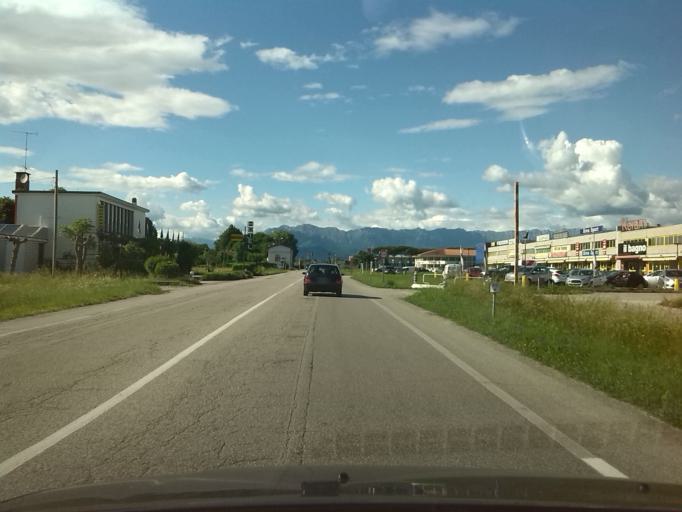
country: IT
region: Friuli Venezia Giulia
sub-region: Provincia di Udine
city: Feletto Umberto
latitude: 46.1053
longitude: 13.2291
